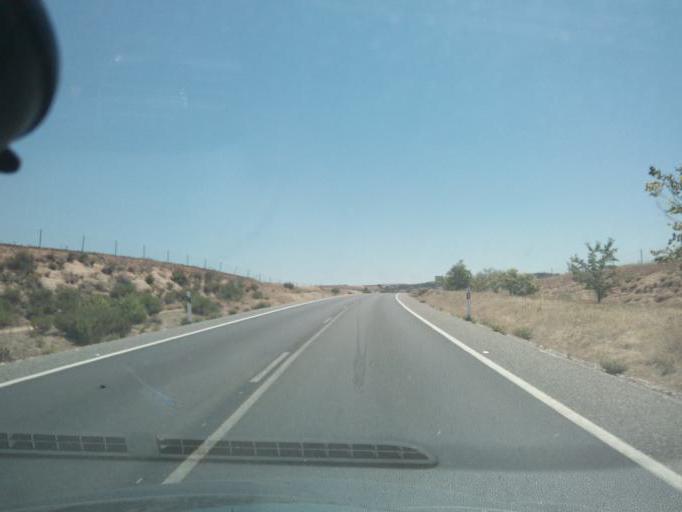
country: ES
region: Madrid
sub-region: Provincia de Madrid
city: Cobena
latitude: 40.5722
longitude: -3.5258
